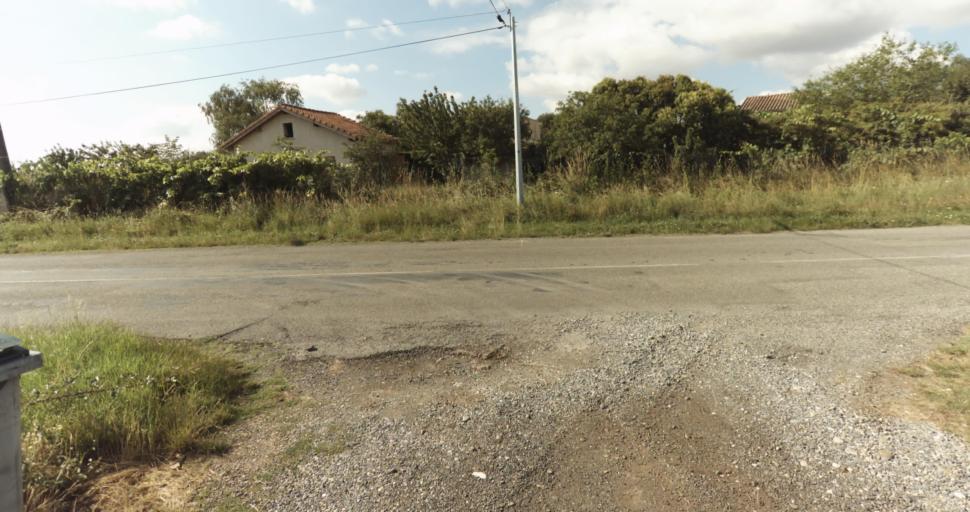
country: FR
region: Midi-Pyrenees
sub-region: Departement de la Haute-Garonne
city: Fontenilles
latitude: 43.5636
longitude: 1.2103
